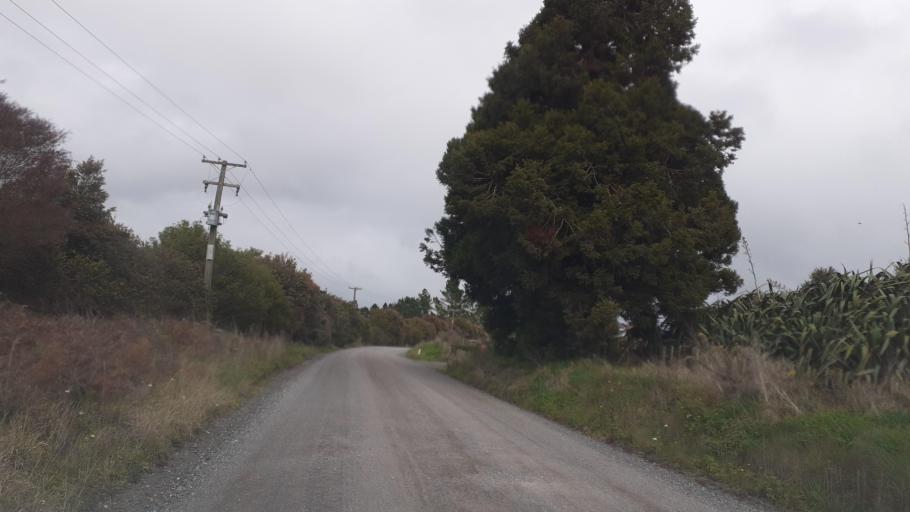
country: NZ
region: Northland
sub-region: Far North District
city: Waimate North
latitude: -35.2439
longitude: 173.7980
